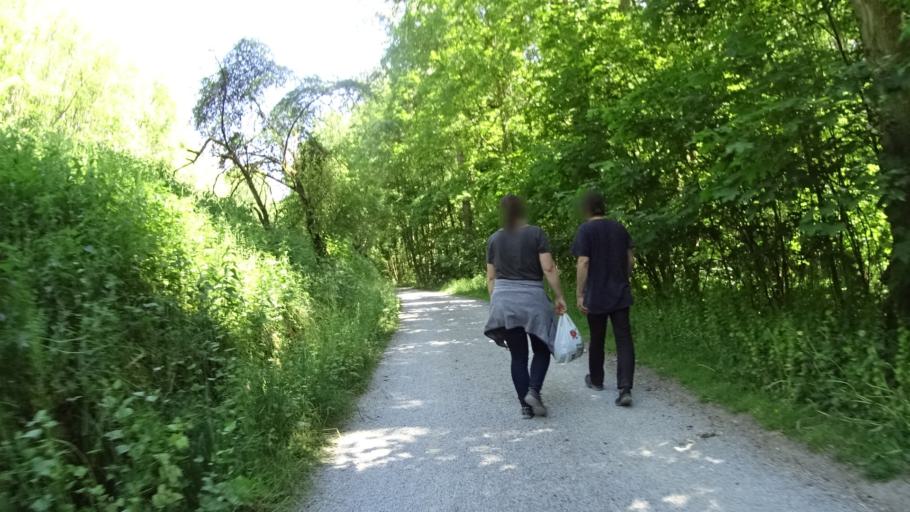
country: DE
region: Bavaria
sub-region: Regierungsbezirk Mittelfranken
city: Rothenburg ob der Tauber
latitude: 49.3623
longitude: 10.1840
